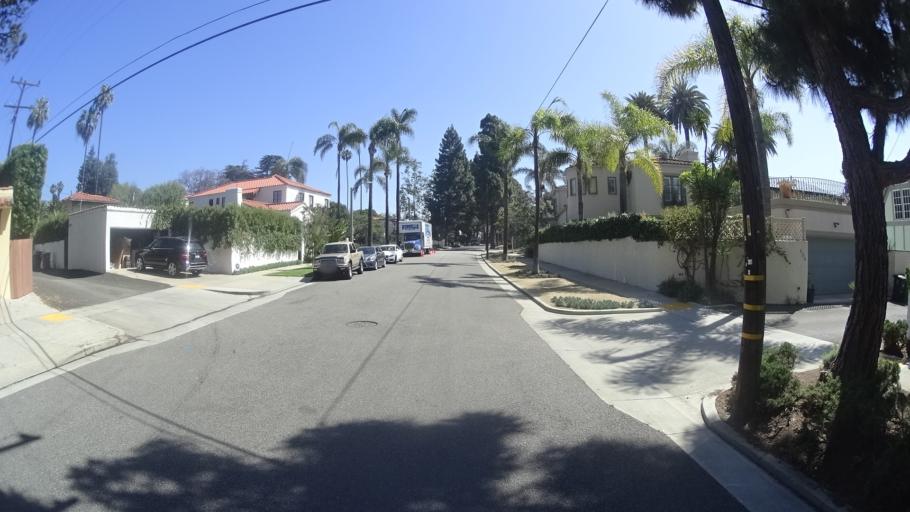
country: US
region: California
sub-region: Los Angeles County
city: Santa Monica
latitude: 34.0376
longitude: -118.4989
